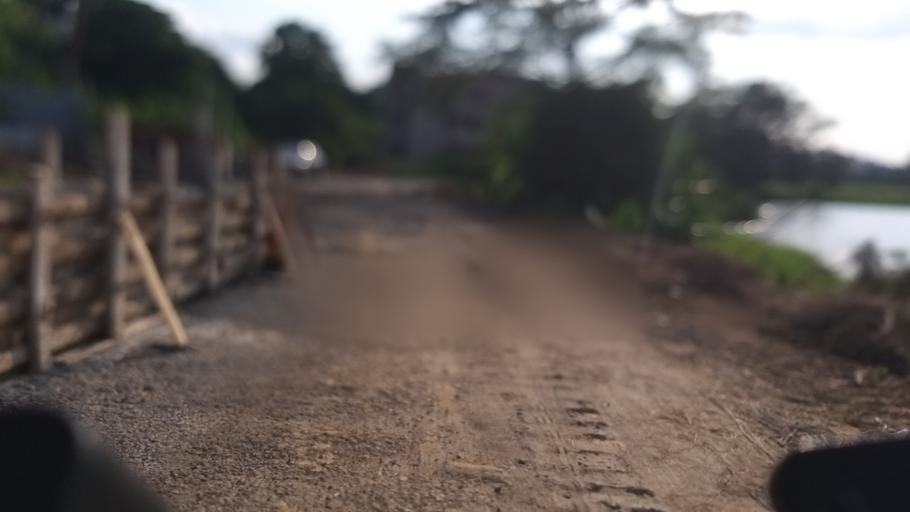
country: HK
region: Yuen Long
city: Yuen Long Kau Hui
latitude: 22.4535
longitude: 114.0395
